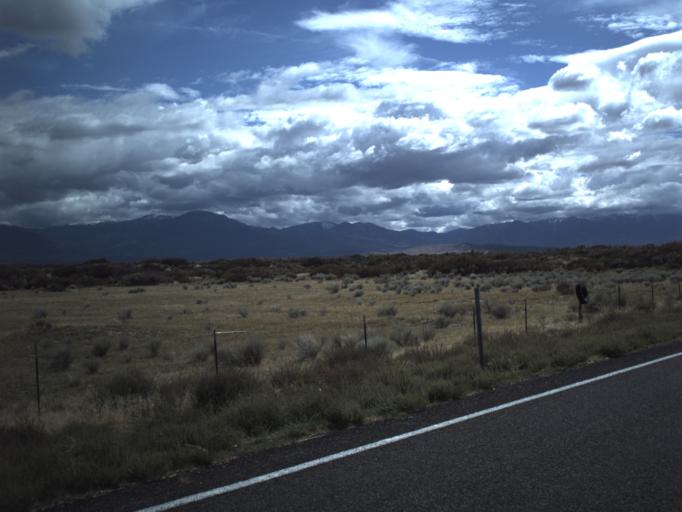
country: US
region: Utah
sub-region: Millard County
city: Fillmore
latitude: 39.1317
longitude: -112.4091
